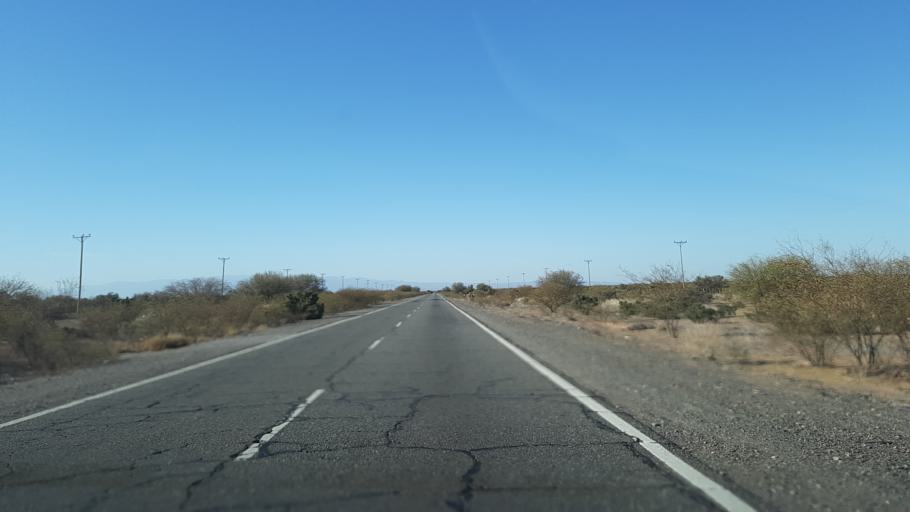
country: AR
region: San Juan
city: Caucete
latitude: -31.6391
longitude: -67.7526
